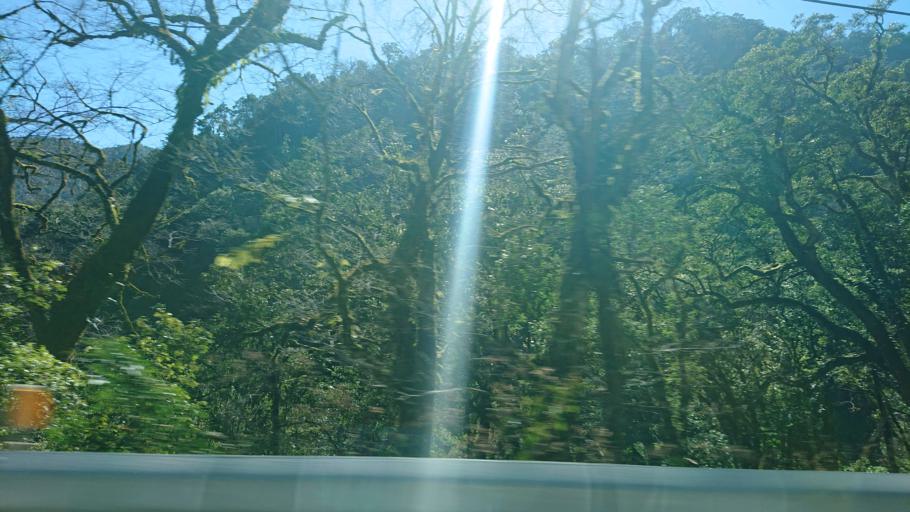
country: TW
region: Taiwan
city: Daxi
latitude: 24.4075
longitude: 121.3579
